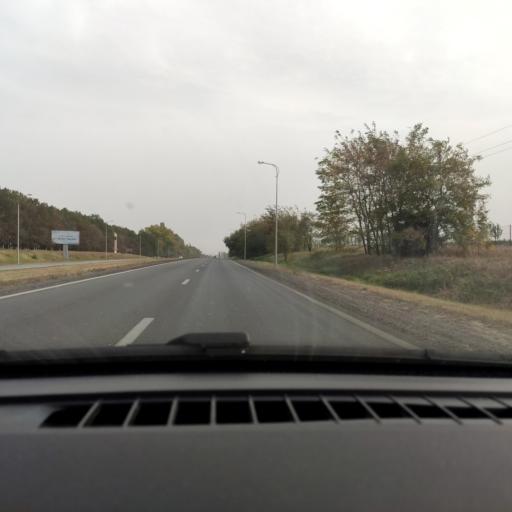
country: RU
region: Belgorod
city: Razumnoye
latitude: 50.6635
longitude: 36.7047
